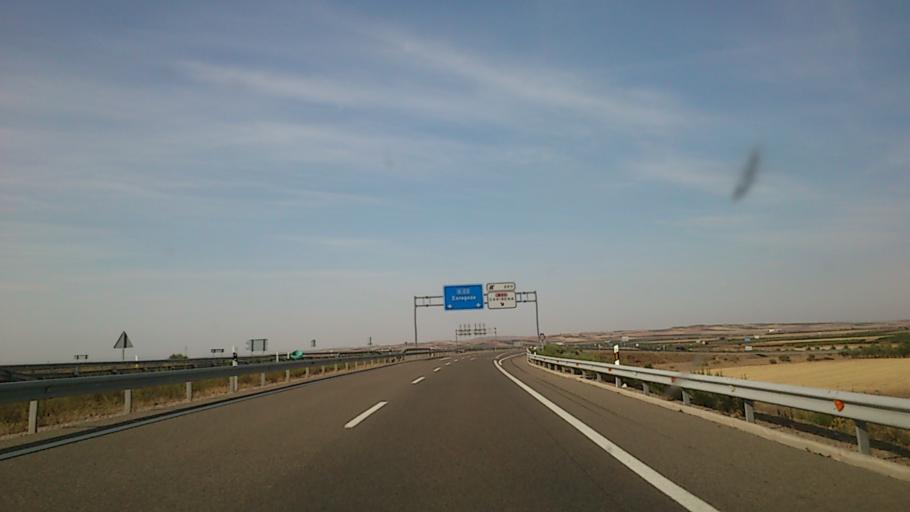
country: ES
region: Aragon
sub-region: Provincia de Zaragoza
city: Carinena
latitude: 41.3656
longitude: -1.2031
